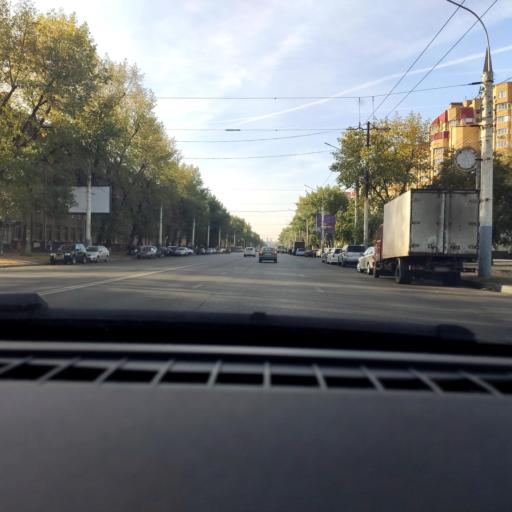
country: RU
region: Voronezj
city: Voronezh
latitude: 51.6454
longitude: 39.2386
